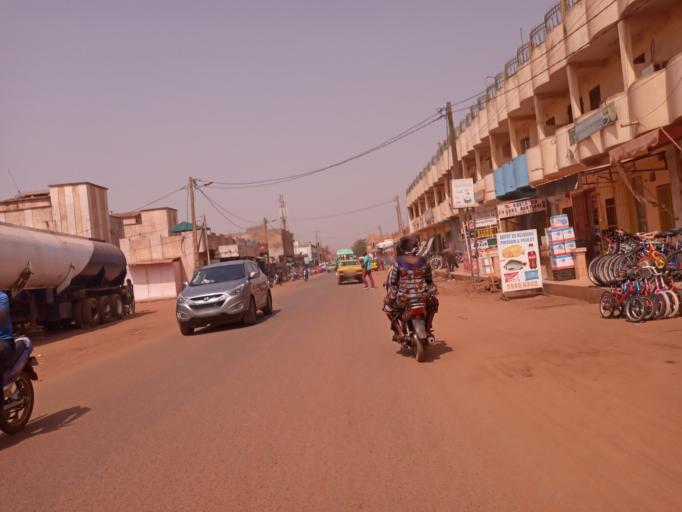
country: ML
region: Bamako
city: Bamako
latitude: 12.5884
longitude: -7.9679
